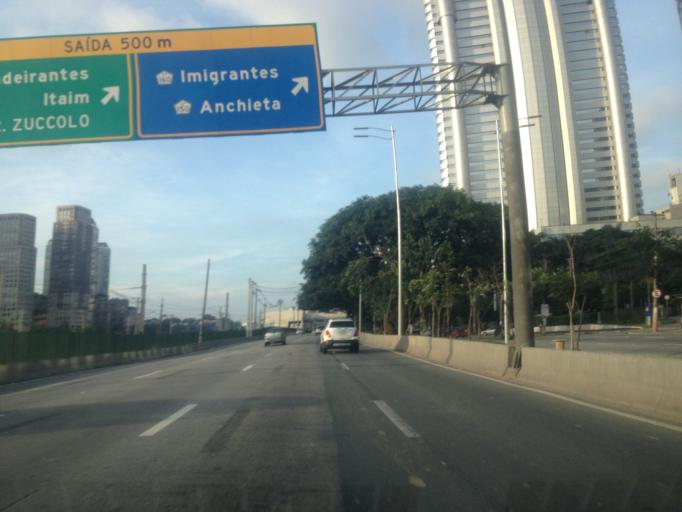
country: BR
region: Sao Paulo
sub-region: Sao Paulo
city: Sao Paulo
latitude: -23.6076
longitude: -46.6976
